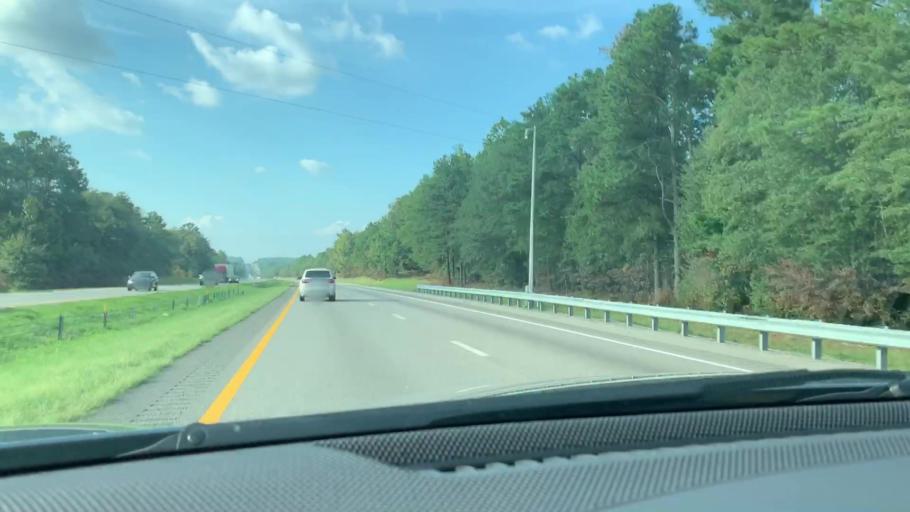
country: US
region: South Carolina
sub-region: Calhoun County
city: Oak Grove
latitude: 33.7095
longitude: -80.9196
